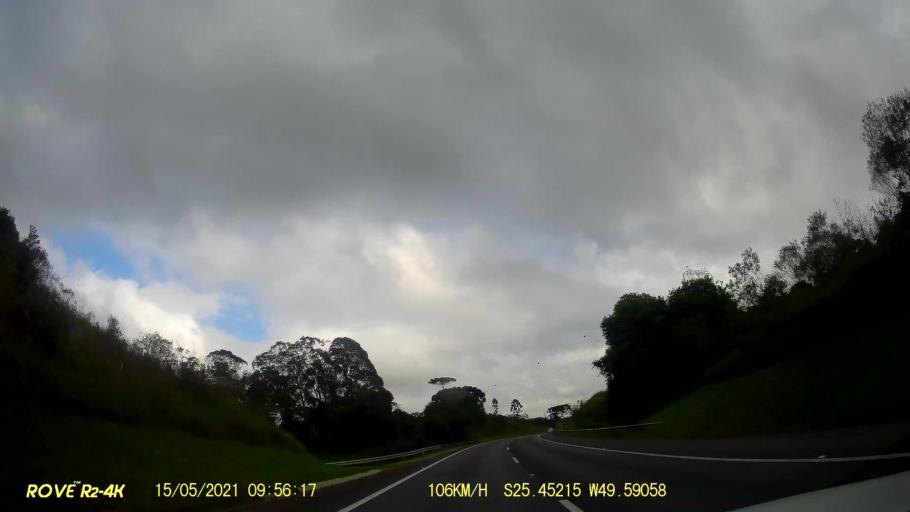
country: BR
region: Parana
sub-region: Campo Largo
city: Campo Largo
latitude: -25.4526
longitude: -49.5921
